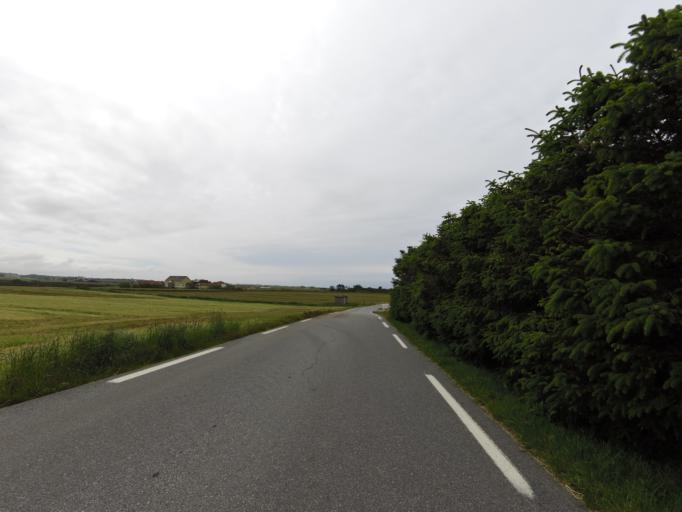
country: NO
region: Rogaland
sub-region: Klepp
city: Kleppe
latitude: 58.8149
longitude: 5.5567
